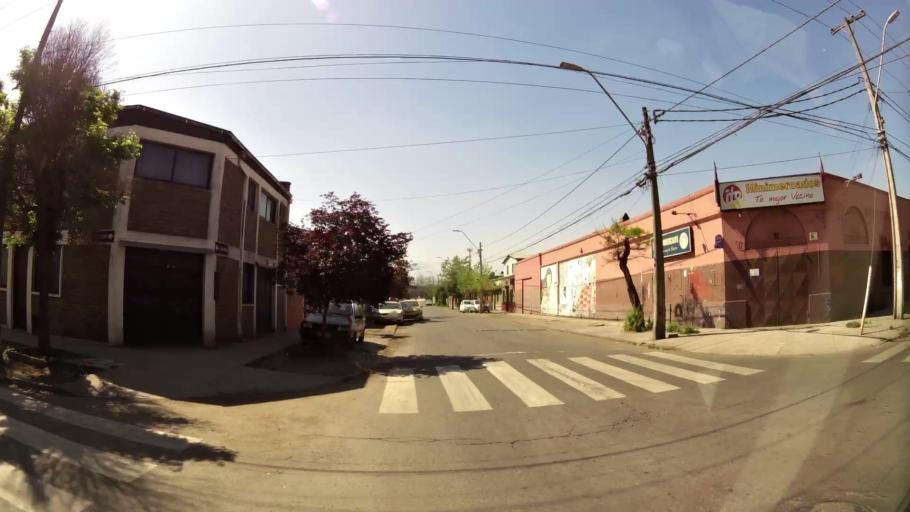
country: CL
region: Santiago Metropolitan
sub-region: Provincia de Santiago
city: Lo Prado
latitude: -33.4153
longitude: -70.6825
